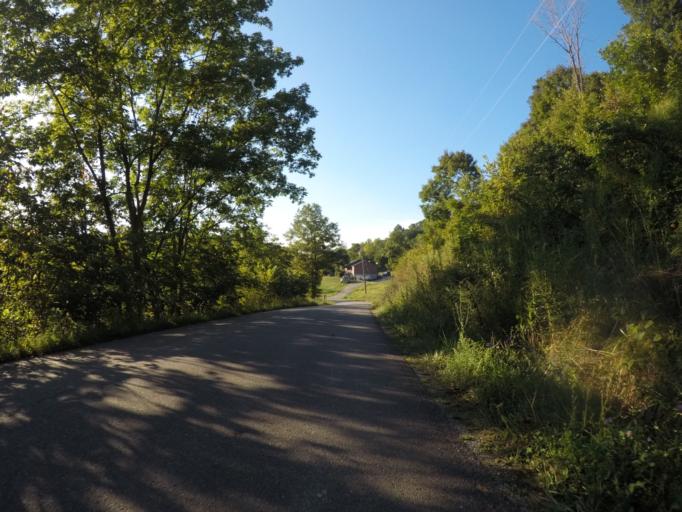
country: US
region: Ohio
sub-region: Lawrence County
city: Coal Grove
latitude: 38.5395
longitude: -82.5481
